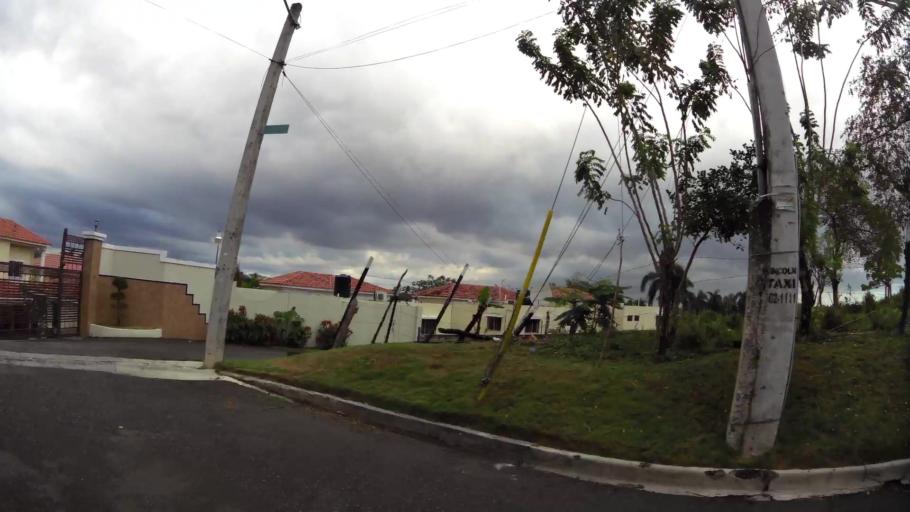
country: DO
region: Nacional
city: Santo Domingo
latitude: 18.5148
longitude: -69.9629
